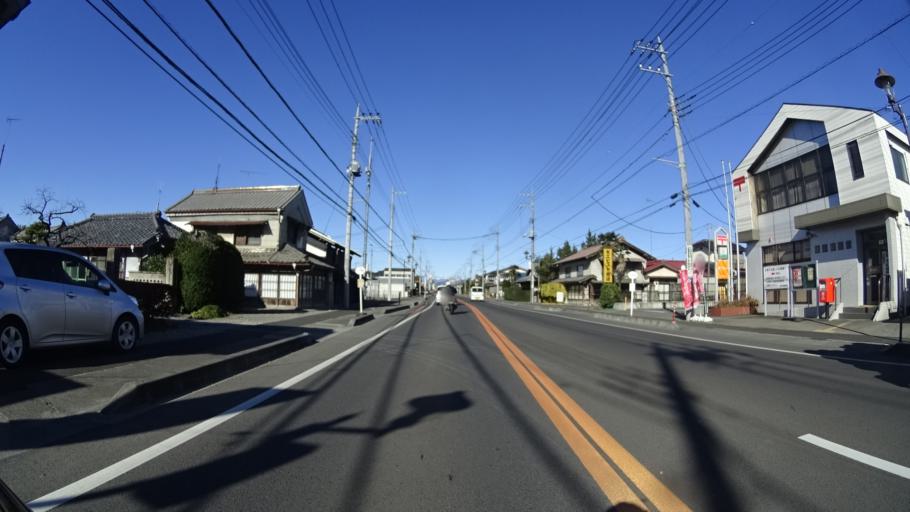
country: JP
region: Tochigi
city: Kanuma
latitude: 36.5070
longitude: 139.7514
